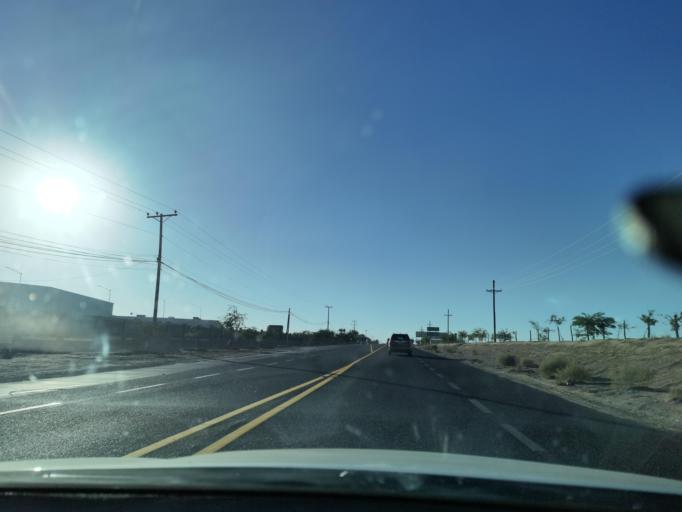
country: MX
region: Baja California
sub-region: Mexicali
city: Islas Agrarias Grupo A
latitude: 32.6354
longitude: -115.2789
